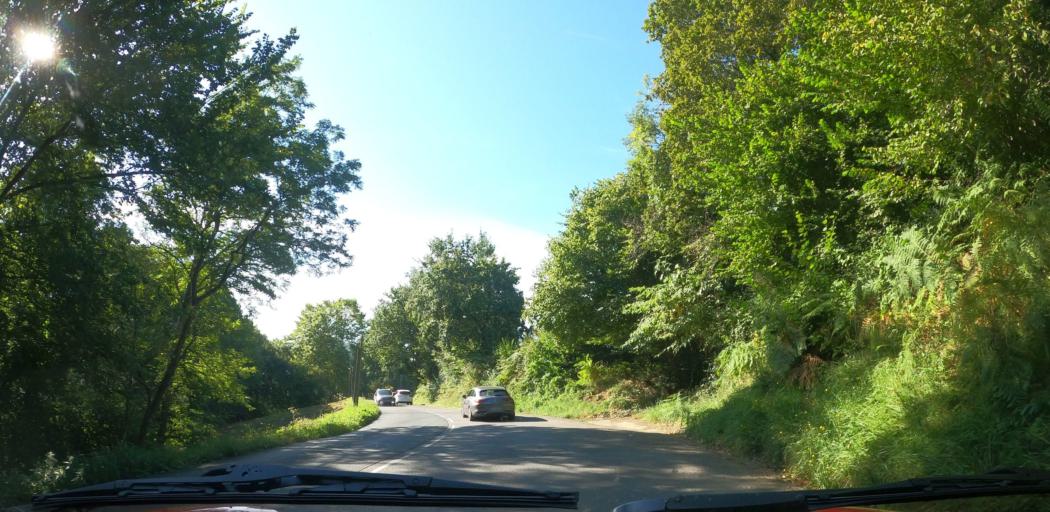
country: FR
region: Aquitaine
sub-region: Departement des Pyrenees-Atlantiques
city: Saint-Pee-sur-Nivelle
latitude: 43.3683
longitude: -1.5451
